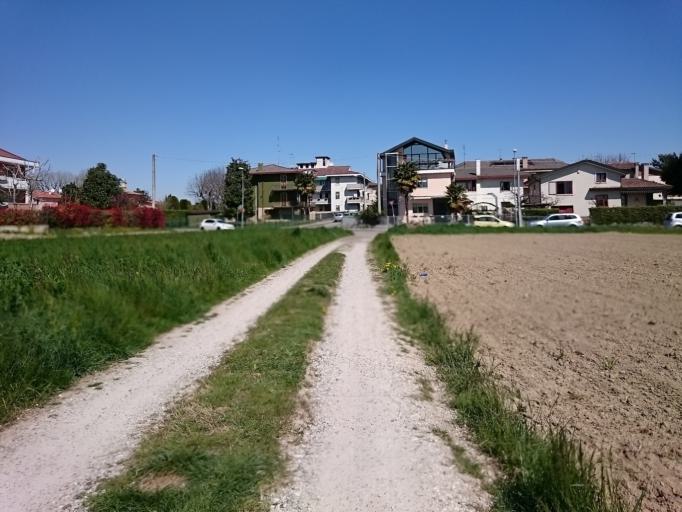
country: IT
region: Veneto
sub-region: Provincia di Padova
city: Padova
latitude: 45.3816
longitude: 11.8945
